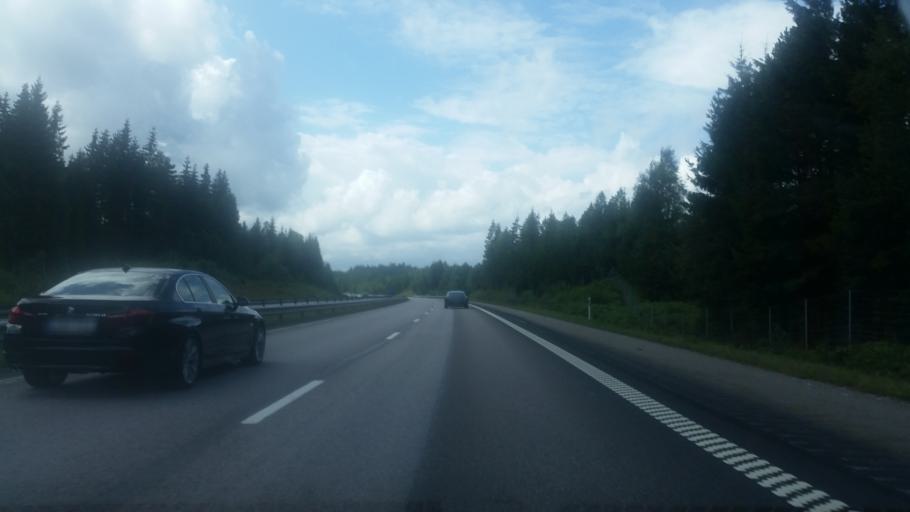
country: SE
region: Vaestra Goetaland
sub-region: Bollebygds Kommun
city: Bollebygd
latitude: 57.6711
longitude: 12.6276
